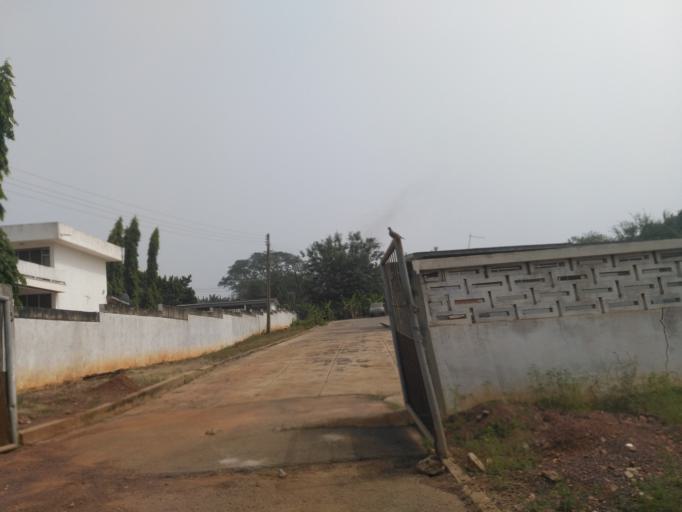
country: GH
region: Ashanti
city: Kumasi
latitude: 6.6764
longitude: -1.6324
